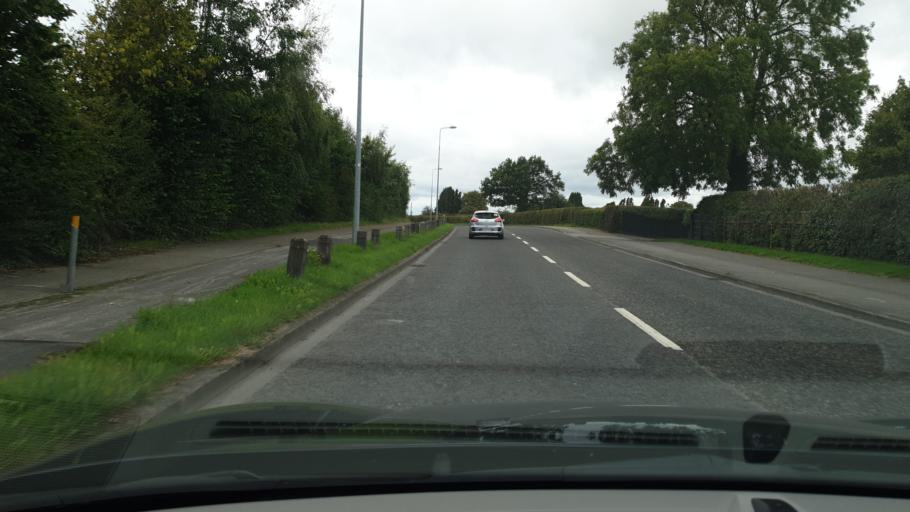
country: IE
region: Leinster
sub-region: Kildare
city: Naas
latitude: 53.2184
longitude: -6.6829
